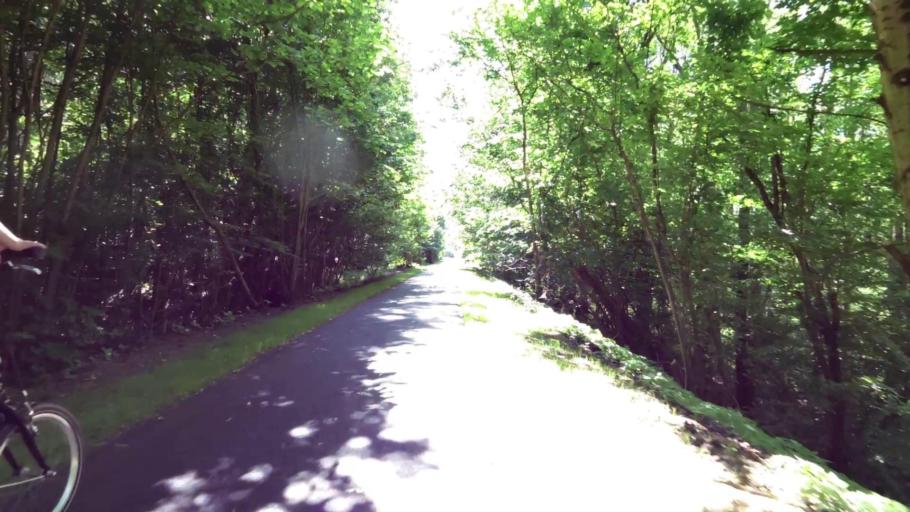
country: PL
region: West Pomeranian Voivodeship
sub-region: Powiat gryfinski
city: Gryfino
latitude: 53.2259
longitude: 14.5319
